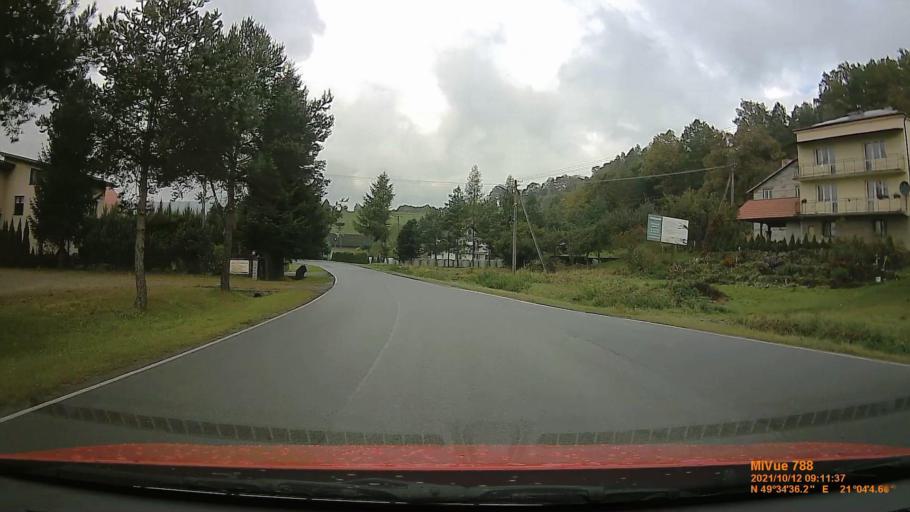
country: PL
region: Lesser Poland Voivodeship
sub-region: Powiat gorlicki
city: Ropa
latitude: 49.5768
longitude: 21.0681
